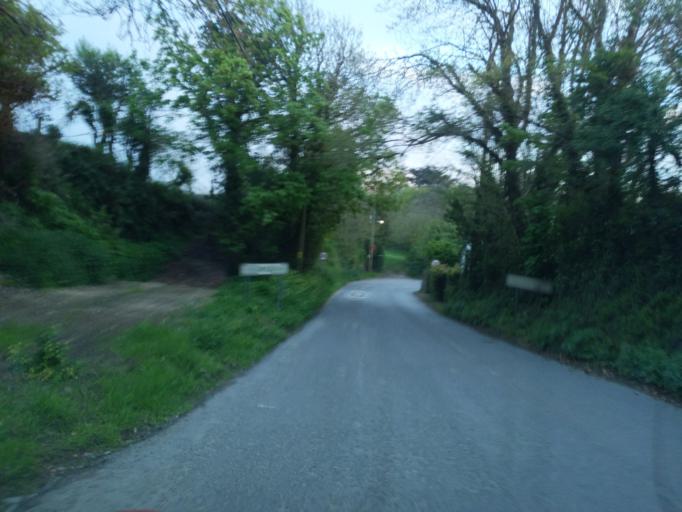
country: GB
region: England
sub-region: Cornwall
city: Polzeath
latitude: 50.5580
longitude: -4.8828
